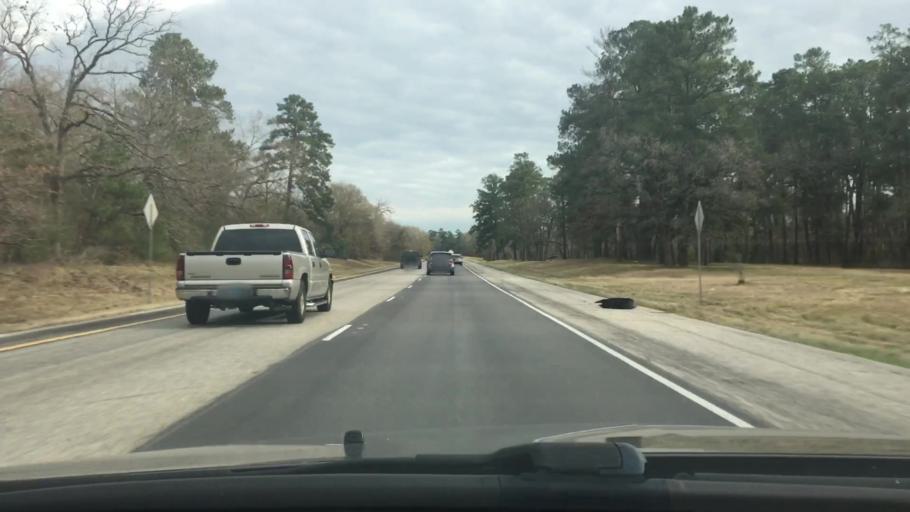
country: US
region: Texas
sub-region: Walker County
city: Huntsville
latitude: 30.7998
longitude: -95.6832
